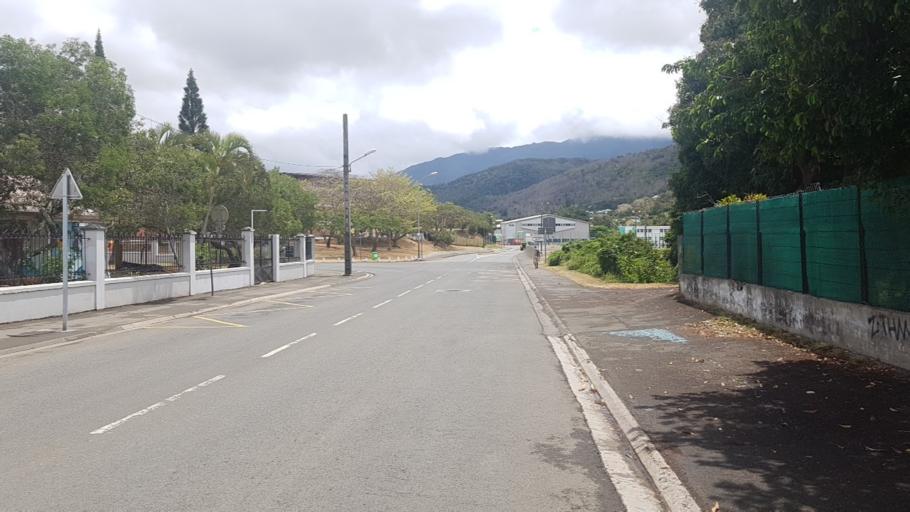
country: NC
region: South Province
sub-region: Dumbea
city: Dumbea
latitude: -22.2087
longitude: 166.4745
